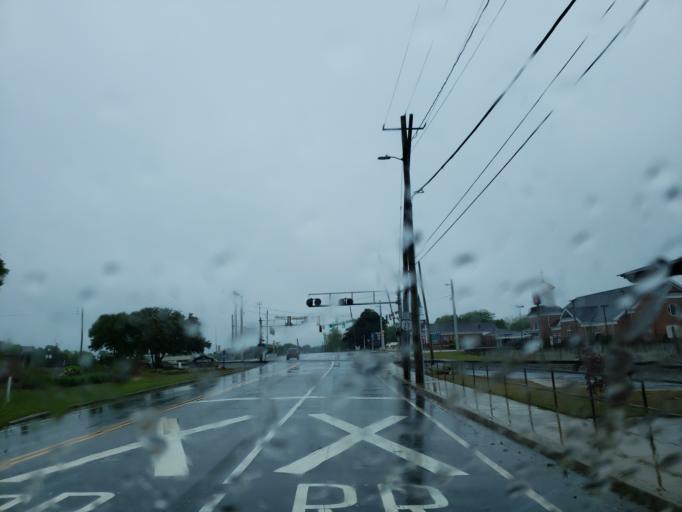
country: US
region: Georgia
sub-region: Haralson County
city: Bremen
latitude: 33.7203
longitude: -85.1468
